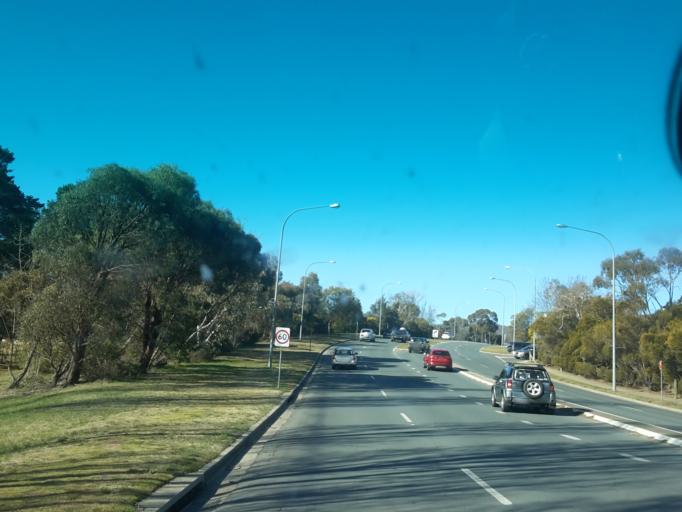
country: AU
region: New South Wales
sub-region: Snowy River
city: Jindabyne
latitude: -36.4147
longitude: 148.6191
